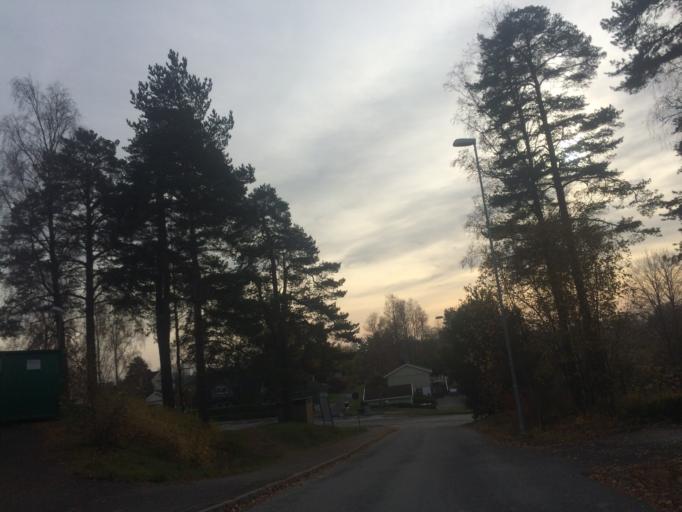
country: NO
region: Akershus
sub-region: Ski
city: Ski
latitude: 59.7262
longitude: 10.8432
